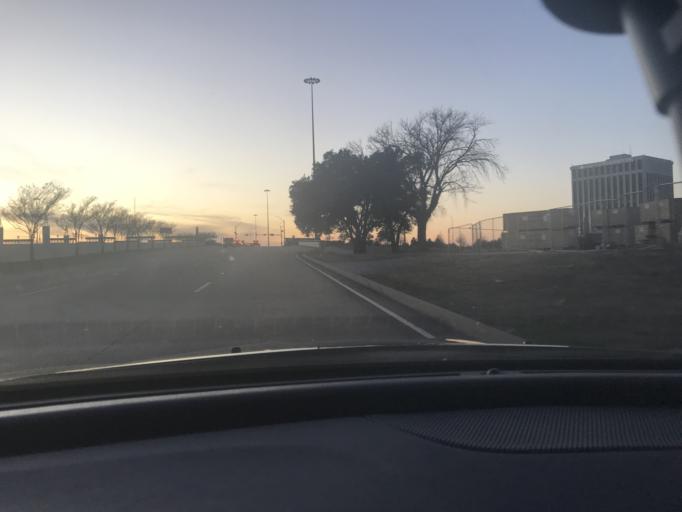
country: US
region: Texas
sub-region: Tarrant County
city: Arlington
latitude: 32.7604
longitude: -97.0995
